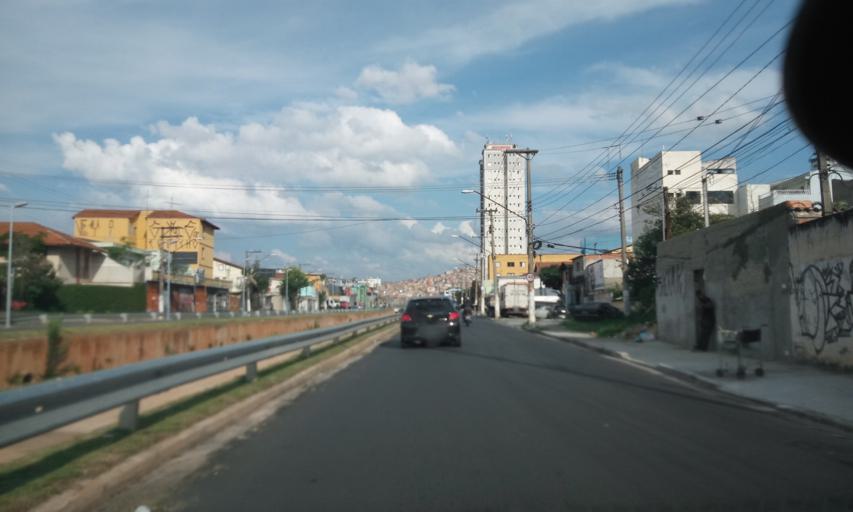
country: BR
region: Sao Paulo
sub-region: Sao Bernardo Do Campo
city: Sao Bernardo do Campo
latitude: -23.7037
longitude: -46.5398
